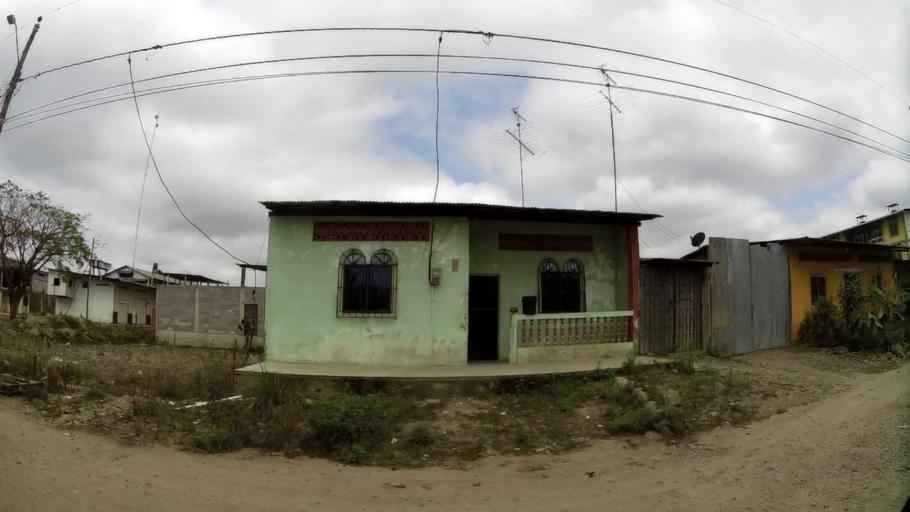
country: EC
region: Guayas
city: Naranjal
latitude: -2.6799
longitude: -79.6184
